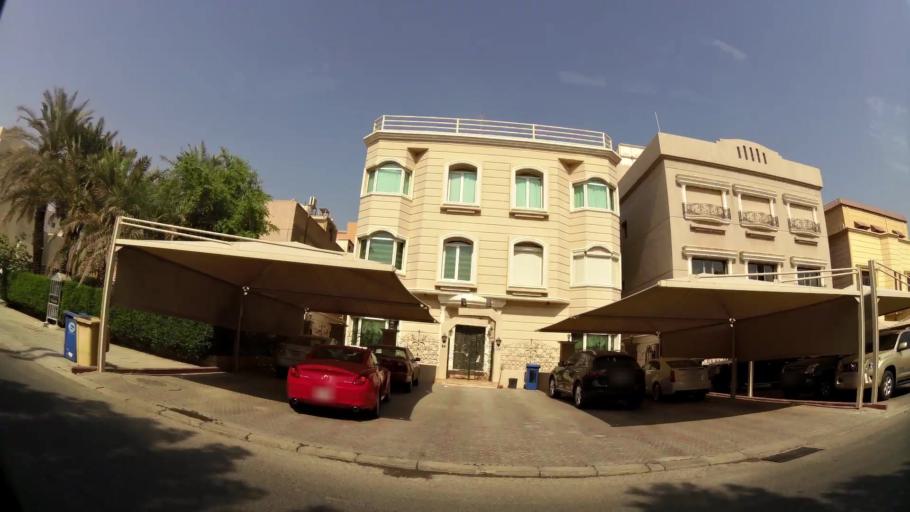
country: KW
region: Muhafazat Hawalli
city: Hawalli
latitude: 29.3481
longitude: 48.0235
